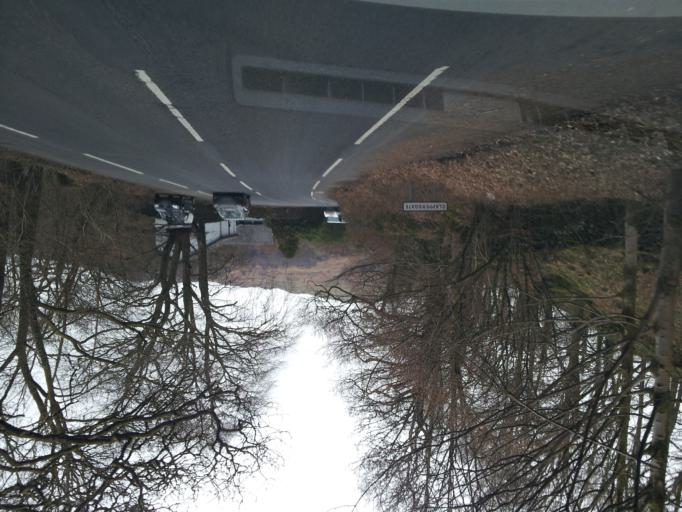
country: GB
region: England
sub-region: Cumbria
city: Ambleside
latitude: 54.4220
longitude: -2.9817
